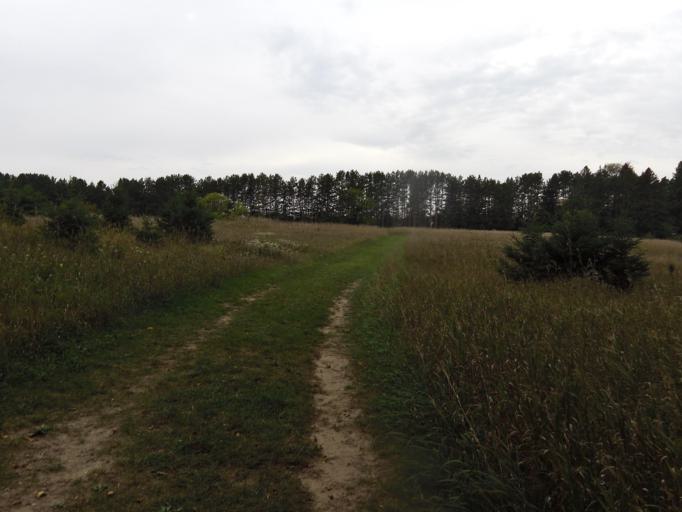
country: US
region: Minnesota
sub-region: Washington County
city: Afton
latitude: 44.8706
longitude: -92.7798
